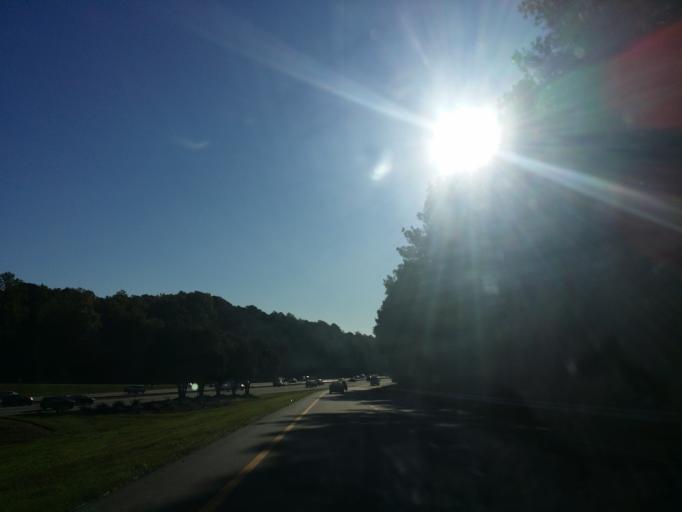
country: US
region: North Carolina
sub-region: Wake County
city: Cary
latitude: 35.8307
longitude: -78.7632
